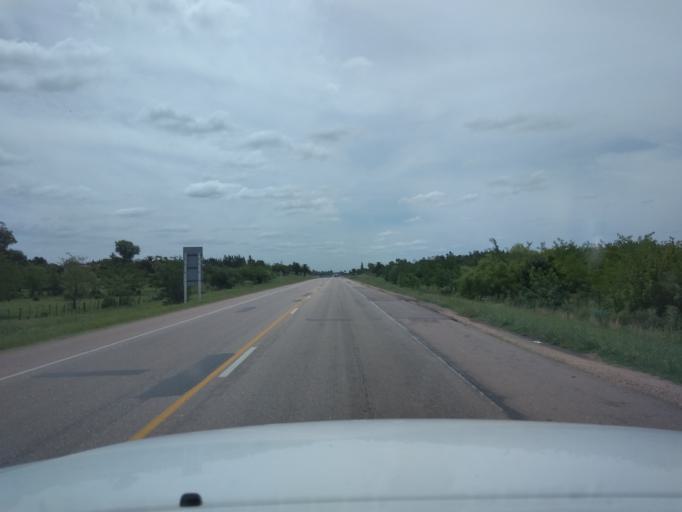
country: UY
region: Canelones
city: Canelones
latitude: -34.5185
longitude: -56.2723
